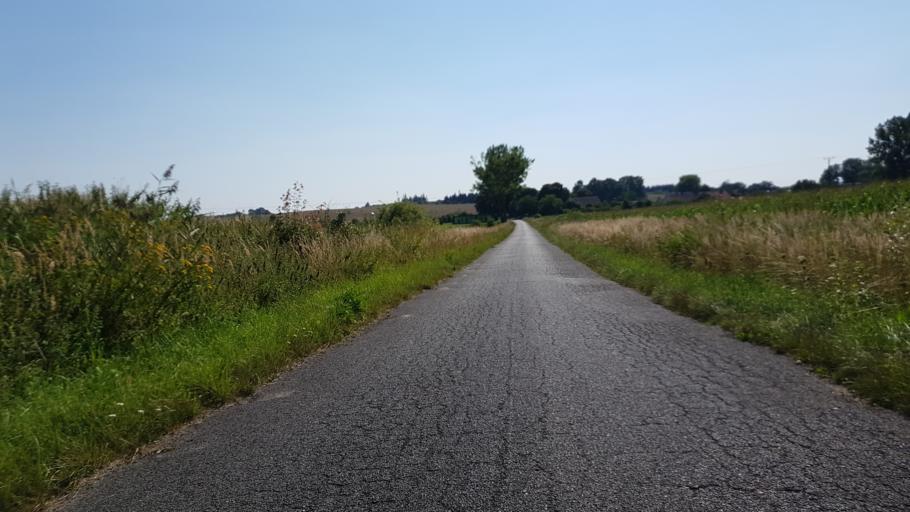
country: PL
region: West Pomeranian Voivodeship
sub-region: Powiat gryfinski
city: Gryfino
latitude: 53.1504
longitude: 14.5149
